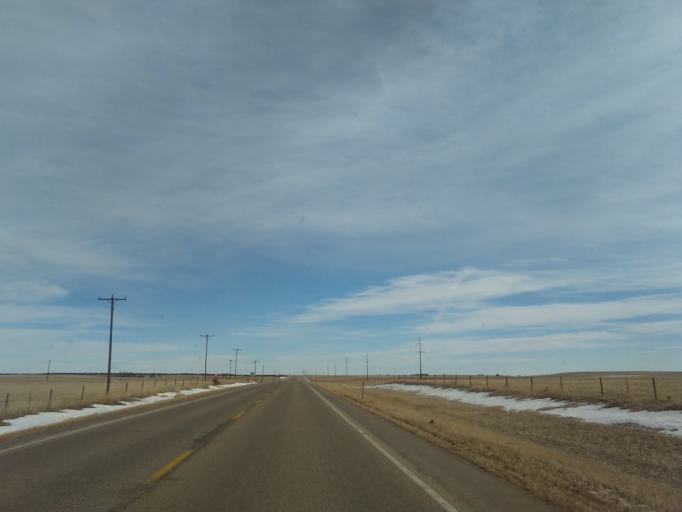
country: US
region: Wyoming
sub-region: Laramie County
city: Ranchettes
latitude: 41.4096
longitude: -104.4389
